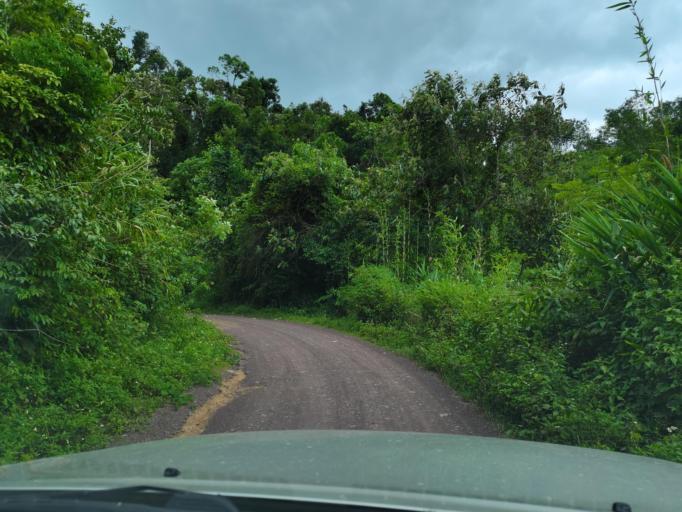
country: LA
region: Loungnamtha
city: Muang Long
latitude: 20.7036
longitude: 101.0124
